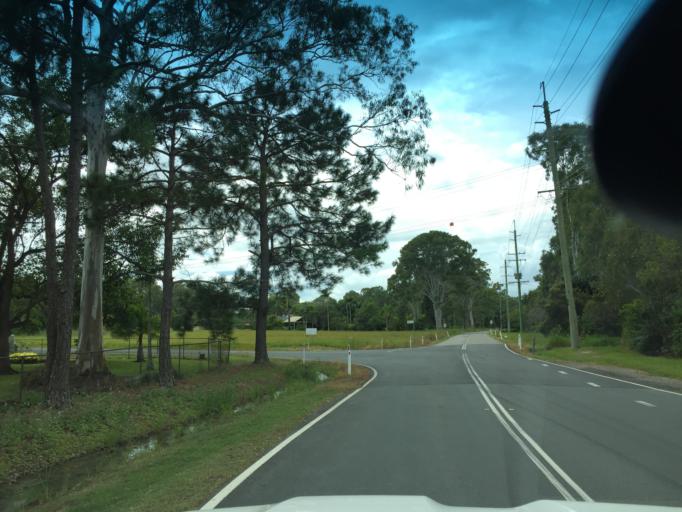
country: AU
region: Queensland
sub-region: Moreton Bay
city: Burpengary
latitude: -27.1687
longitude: 152.9882
